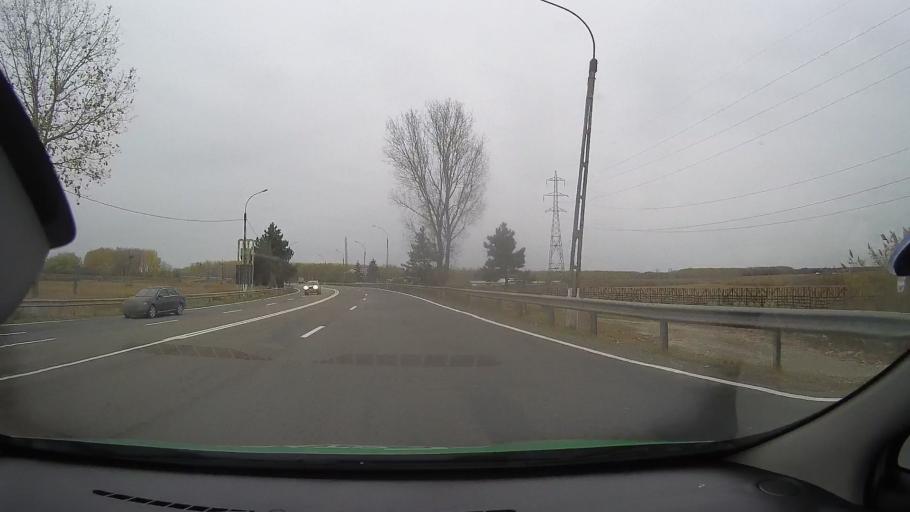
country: RO
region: Ialomita
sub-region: Comuna Giurgeni
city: Giurgeni
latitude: 44.7500
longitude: 27.8925
